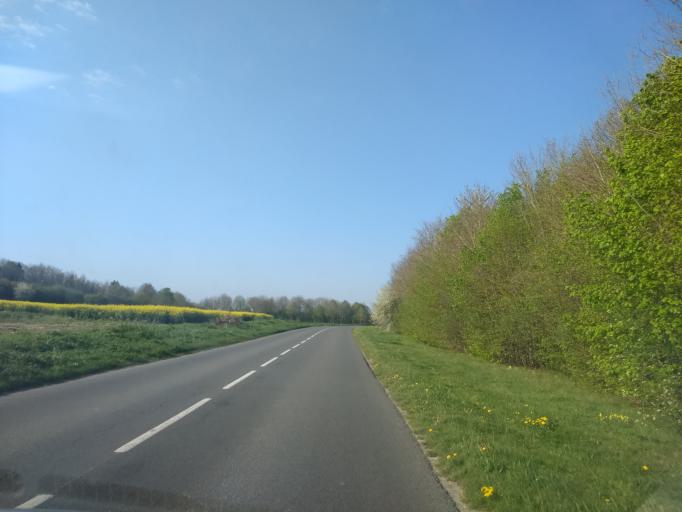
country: FR
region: Picardie
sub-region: Departement de la Somme
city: Rivery
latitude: 49.9291
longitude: 2.3408
